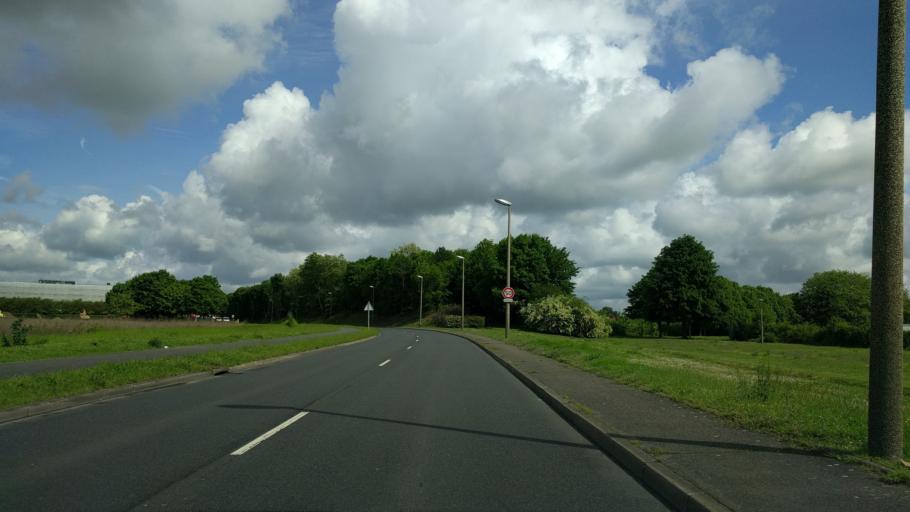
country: FR
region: Ile-de-France
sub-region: Departement de Seine-et-Marne
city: Savigny-le-Temple
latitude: 48.5931
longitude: 2.5911
